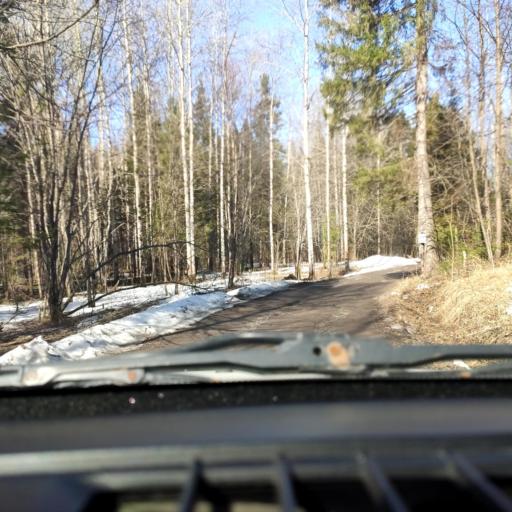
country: RU
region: Perm
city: Kultayevo
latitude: 57.8242
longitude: 55.7878
